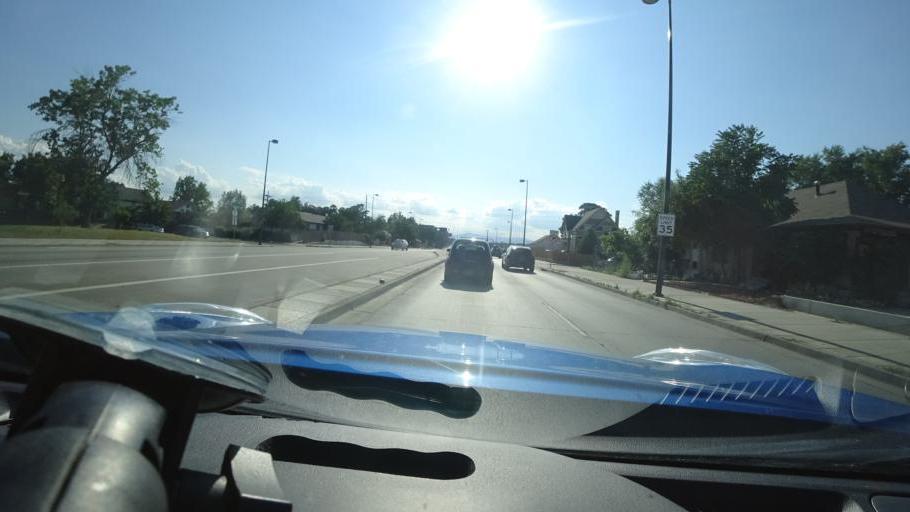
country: US
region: Colorado
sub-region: Arapahoe County
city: Englewood
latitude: 39.6786
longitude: -104.9881
